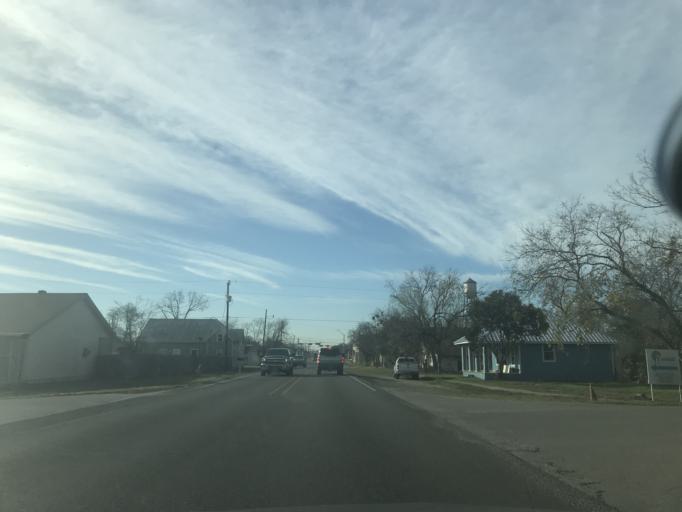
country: US
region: Texas
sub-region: Travis County
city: Manor
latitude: 30.3430
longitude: -97.5573
